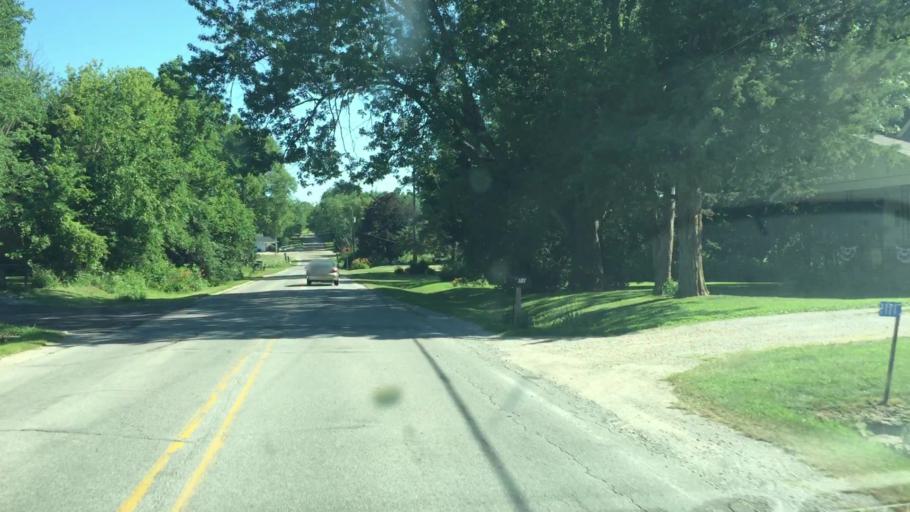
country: US
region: Iowa
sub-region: Linn County
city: Ely
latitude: 41.8503
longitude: -91.6461
